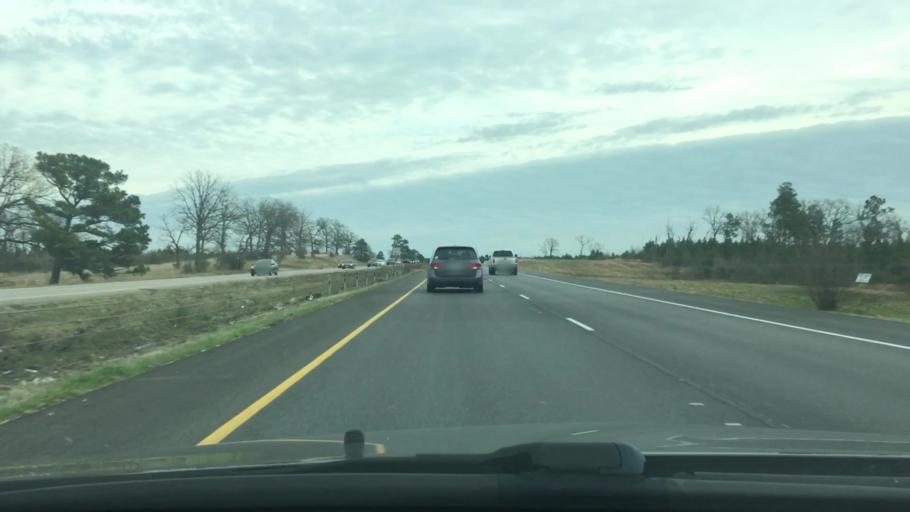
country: US
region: Texas
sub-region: Madison County
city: Madisonville
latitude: 30.8474
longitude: -95.7331
